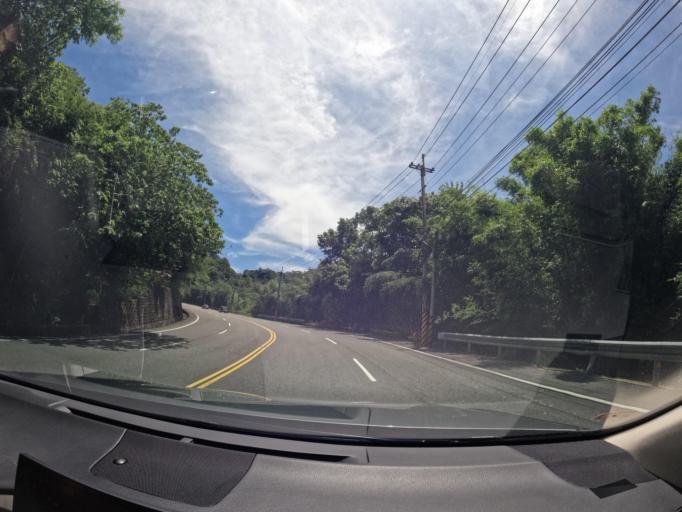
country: TW
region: Taiwan
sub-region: Miaoli
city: Miaoli
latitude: 24.5005
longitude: 120.9039
